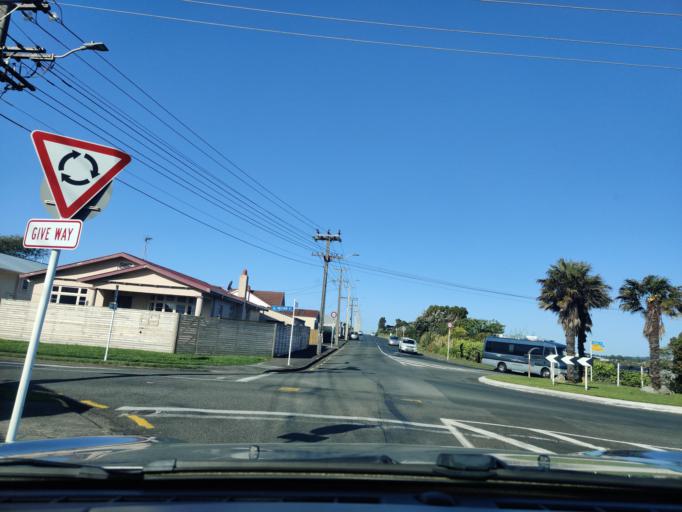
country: NZ
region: Taranaki
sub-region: New Plymouth District
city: New Plymouth
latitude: -39.0483
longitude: 174.1052
